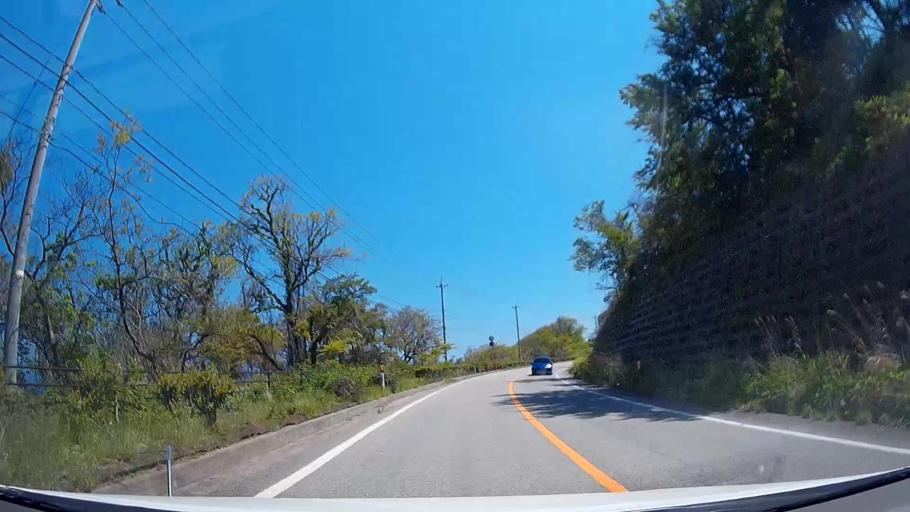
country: JP
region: Ishikawa
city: Nanao
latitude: 37.4213
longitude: 136.9904
